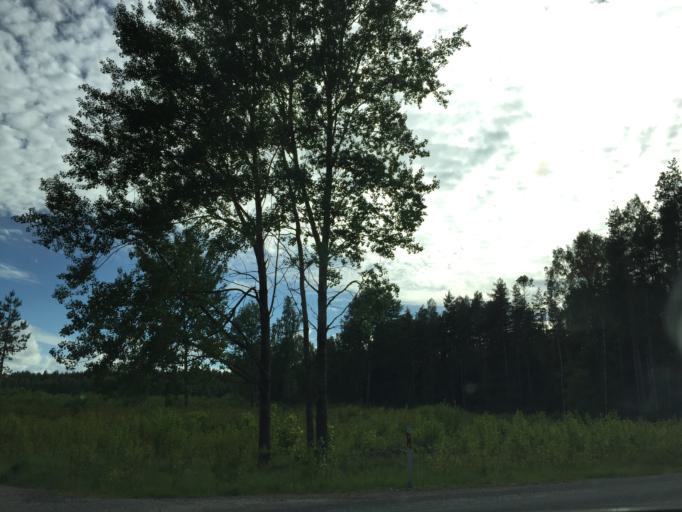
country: LV
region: Dobeles Rajons
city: Dobele
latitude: 56.6577
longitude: 23.1820
